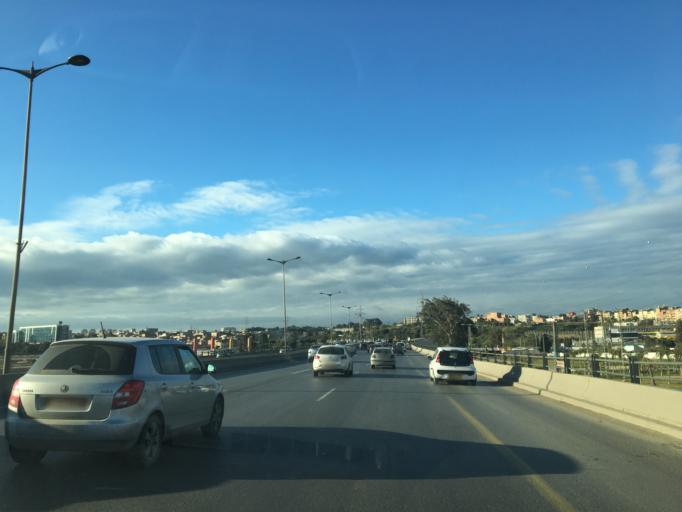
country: DZ
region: Tipaza
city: Baraki
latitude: 36.7037
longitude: 3.1152
